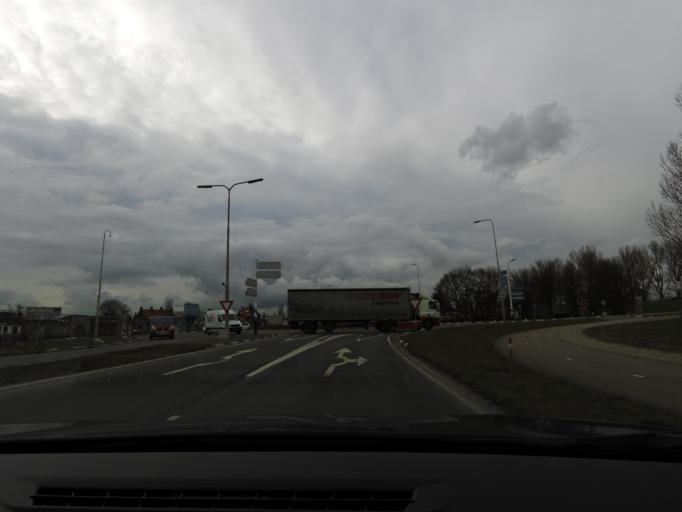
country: NL
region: South Holland
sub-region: Gemeente Gouda
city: Bloemendaal
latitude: 52.0234
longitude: 4.6704
